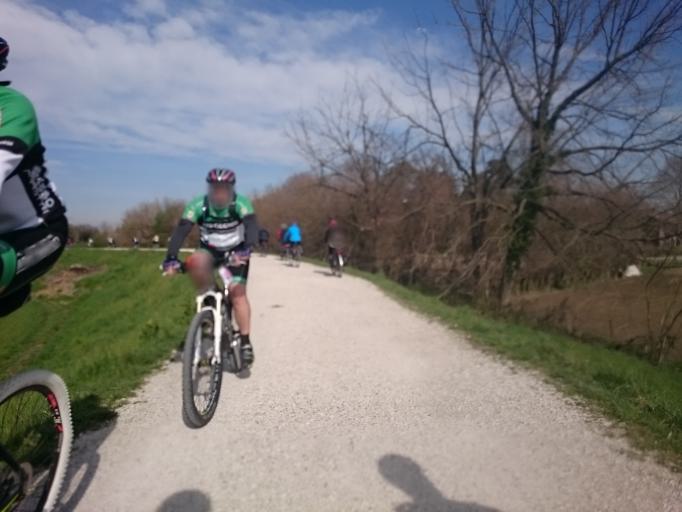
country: IT
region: Veneto
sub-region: Provincia di Padova
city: Tencarola
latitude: 45.3919
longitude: 11.8277
